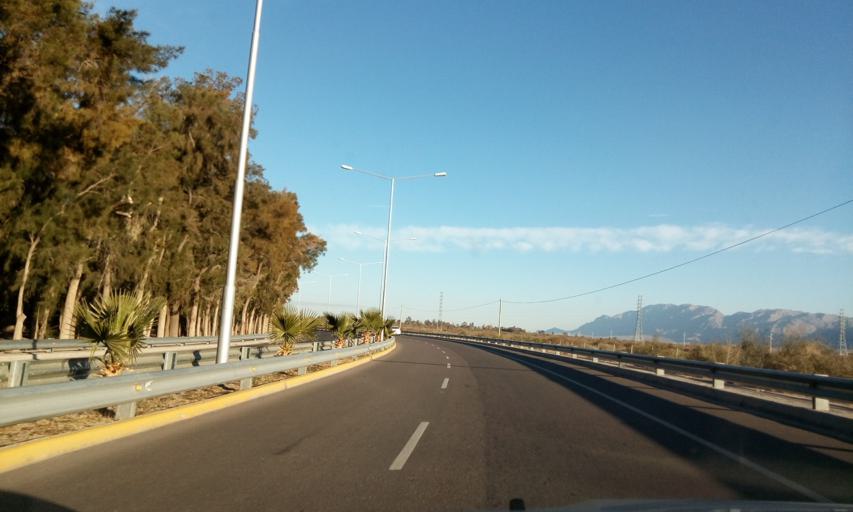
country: AR
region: San Juan
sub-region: Departamento de Rivadavia
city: Rivadavia
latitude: -31.5100
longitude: -68.6453
